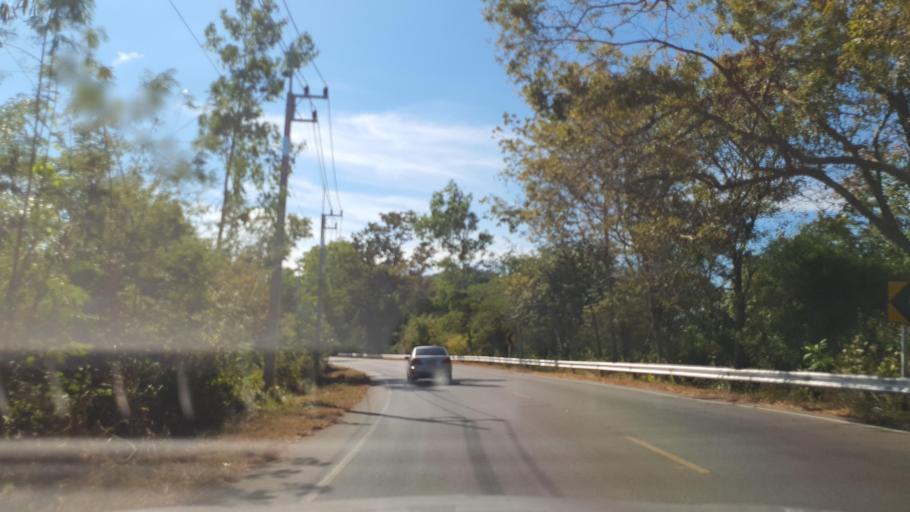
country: TH
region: Kalasin
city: Khao Wong
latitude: 16.7644
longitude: 104.1331
